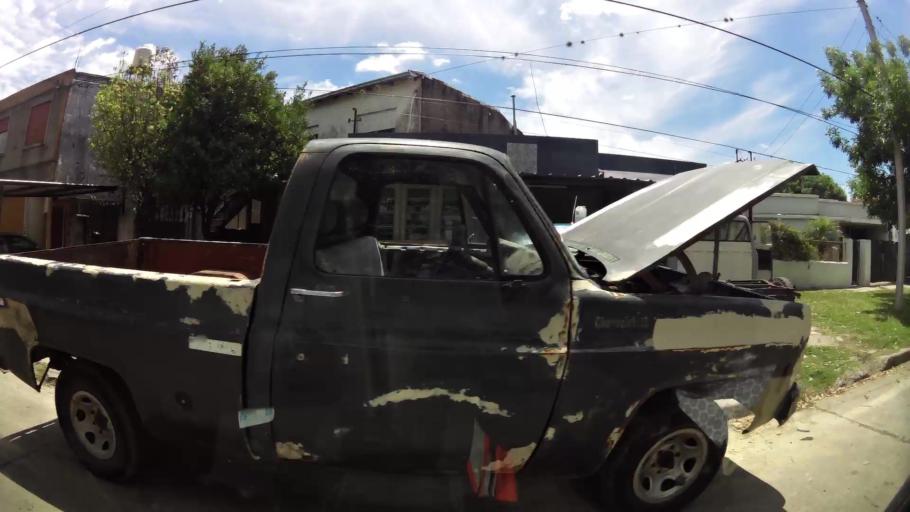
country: AR
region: Santa Fe
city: Gobernador Galvez
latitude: -33.0022
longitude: -60.6218
